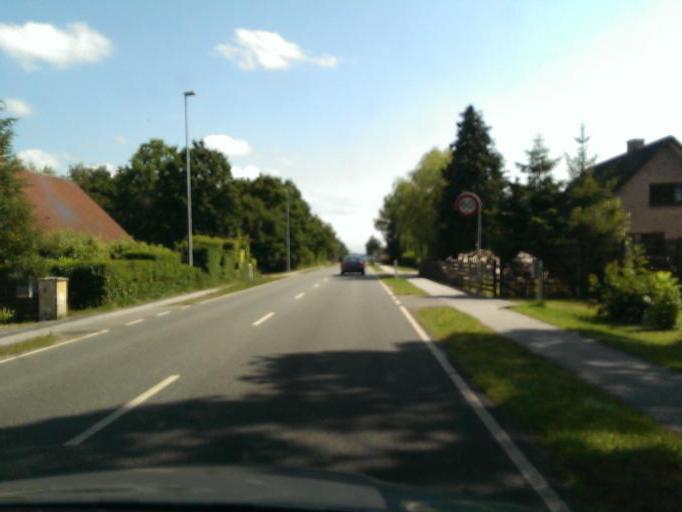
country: DK
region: Central Jutland
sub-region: Syddjurs Kommune
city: Ebeltoft
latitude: 56.2310
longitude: 10.5993
